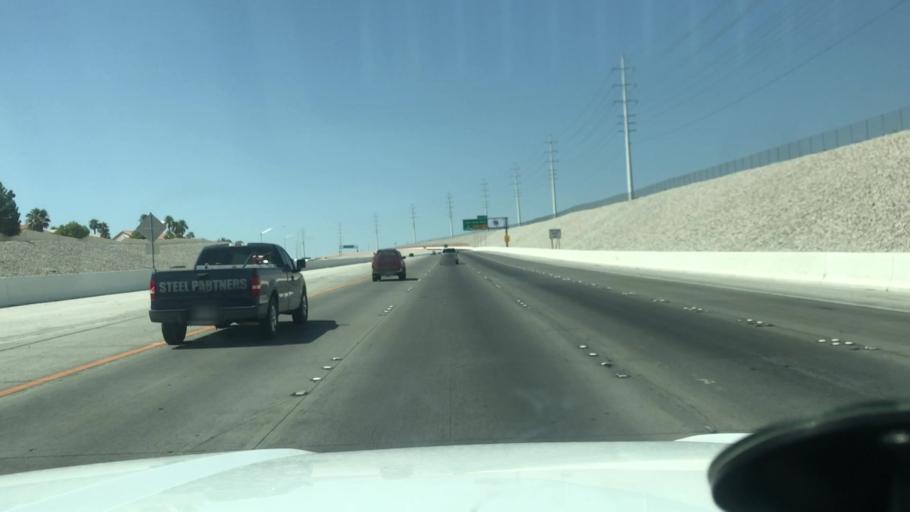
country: US
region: Nevada
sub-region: Clark County
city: Summerlin South
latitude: 36.2125
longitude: -115.3349
